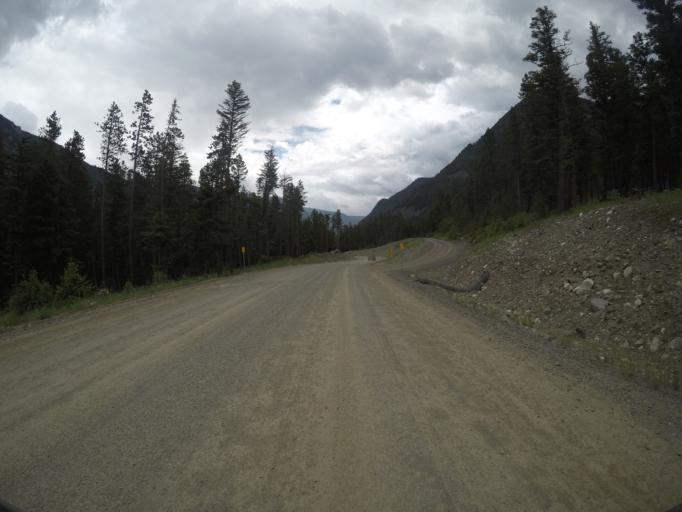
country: US
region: Montana
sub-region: Park County
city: Livingston
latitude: 45.4888
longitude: -110.2182
